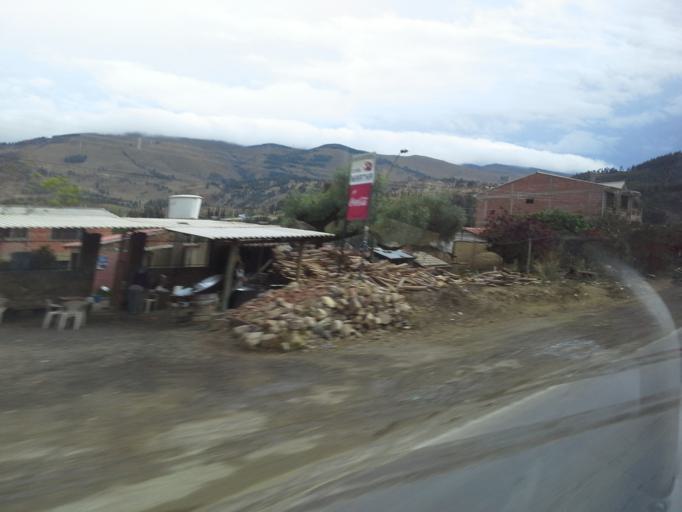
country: BO
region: Cochabamba
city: Colomi
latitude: -17.4200
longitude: -65.9458
